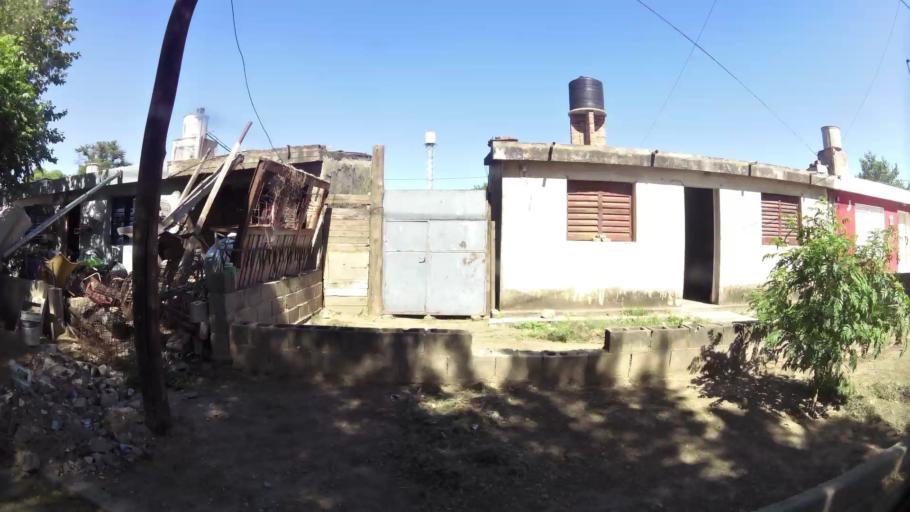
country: AR
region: Cordoba
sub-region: Departamento de Capital
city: Cordoba
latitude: -31.4438
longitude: -64.1321
